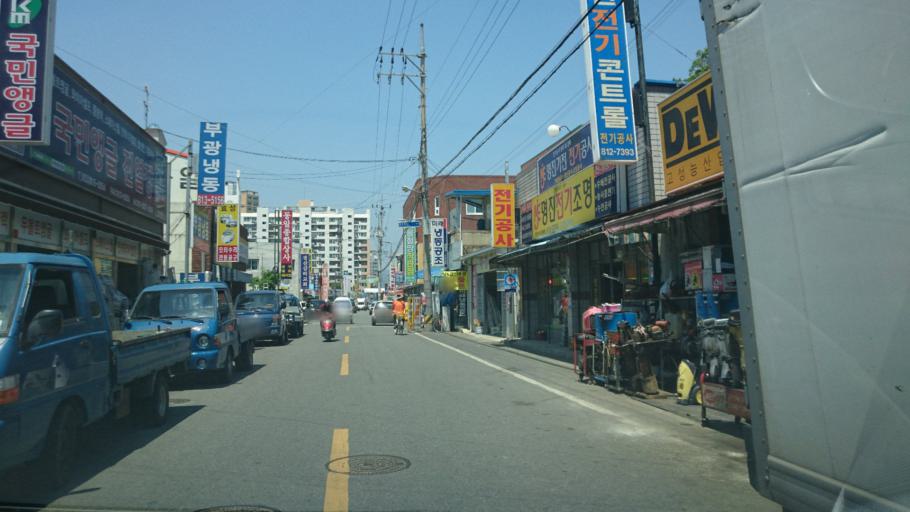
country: KR
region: Gyeongsangbuk-do
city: Gyeongsan-si
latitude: 35.8274
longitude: 128.7382
